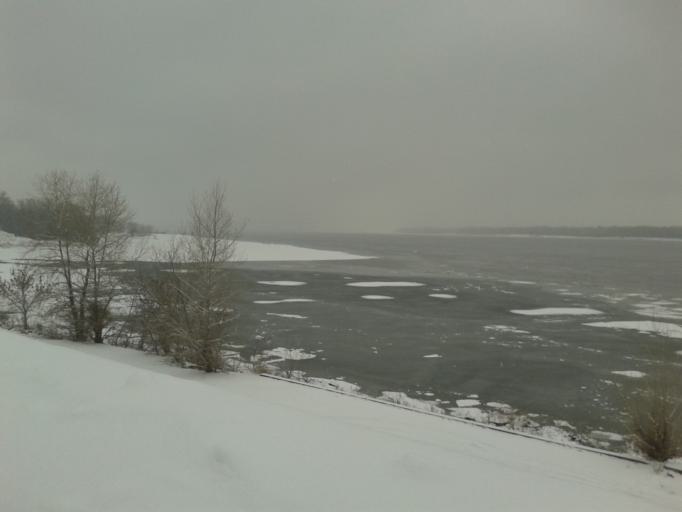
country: RU
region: Volgograd
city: Krasnoslobodsk
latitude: 48.5279
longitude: 44.5587
